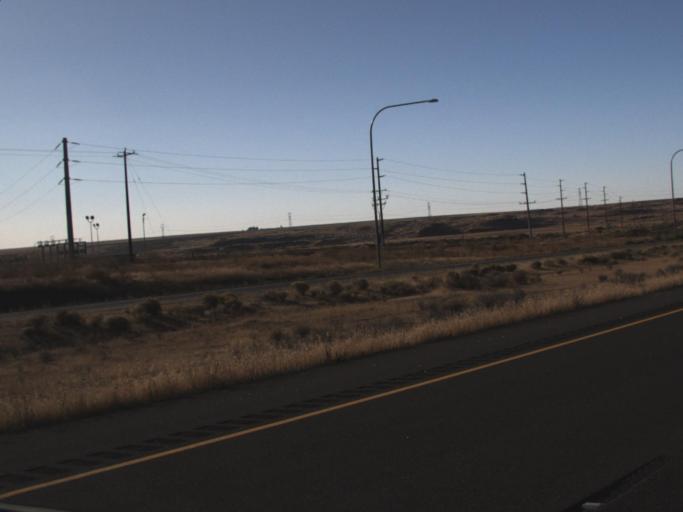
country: US
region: Washington
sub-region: Franklin County
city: Connell
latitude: 46.6597
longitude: -118.8513
